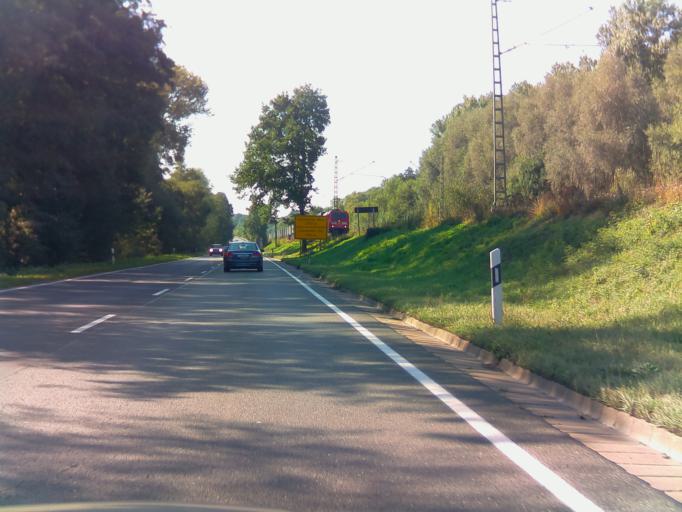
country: DE
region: Bavaria
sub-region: Upper Franconia
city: Michelau
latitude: 50.1534
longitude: 11.1040
